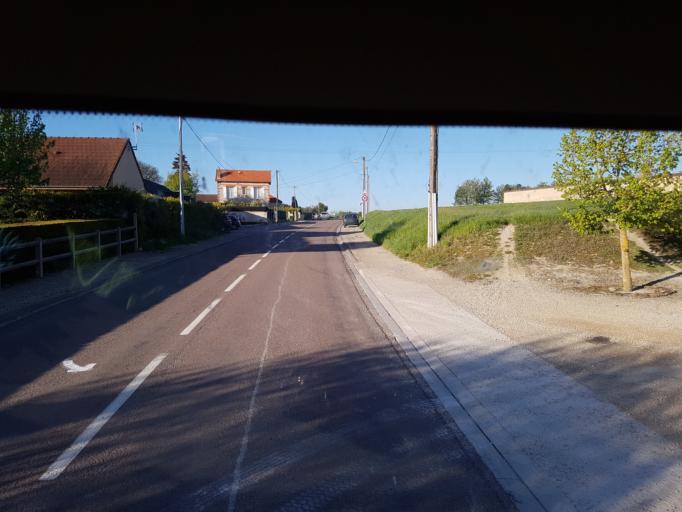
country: FR
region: Champagne-Ardenne
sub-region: Departement de l'Aube
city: Marigny-le-Chatel
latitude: 48.4412
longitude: 3.6823
